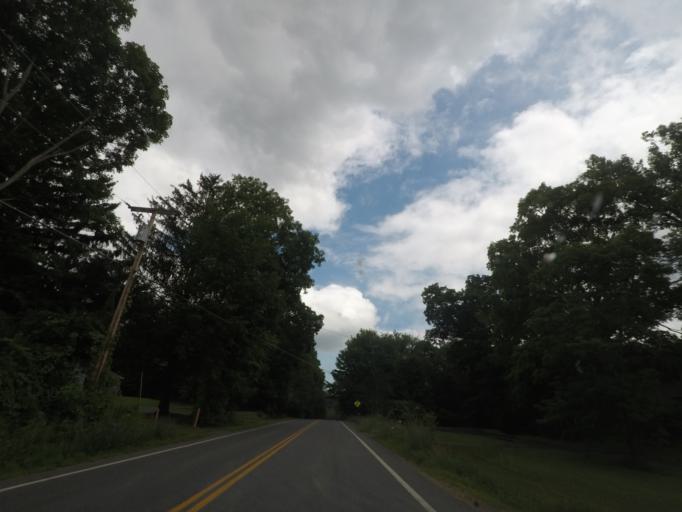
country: US
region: New York
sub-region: Saratoga County
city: Stillwater
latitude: 43.0038
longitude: -73.7013
